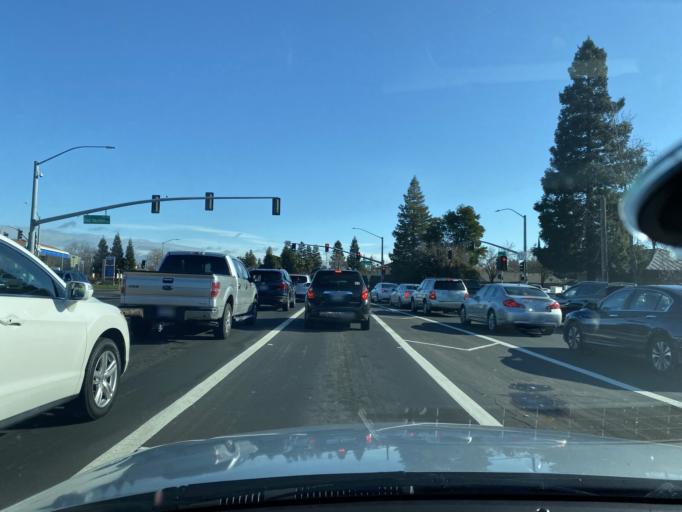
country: US
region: California
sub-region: Sacramento County
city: Elk Grove
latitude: 38.4237
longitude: -121.3909
